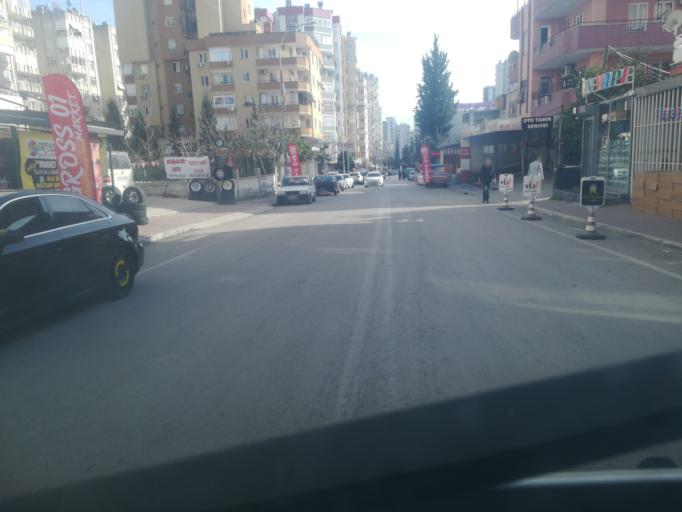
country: TR
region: Adana
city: Adana
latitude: 37.0350
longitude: 35.3125
